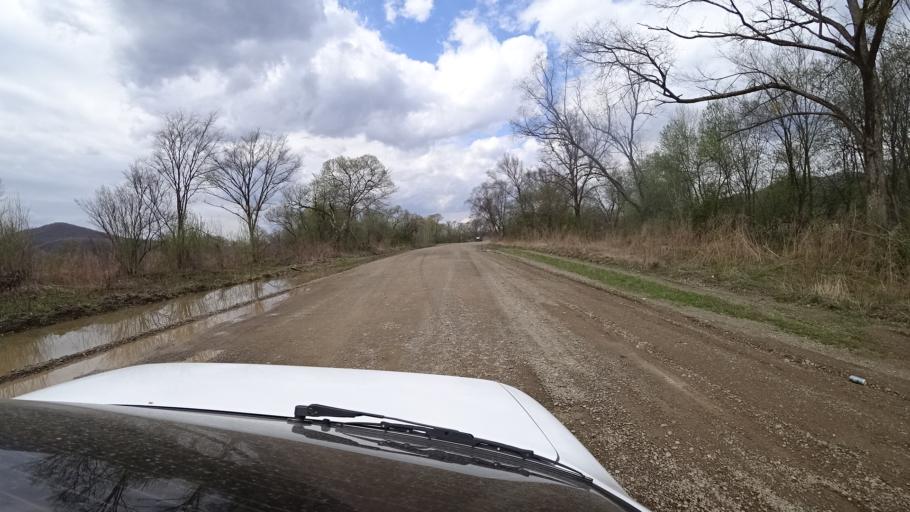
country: RU
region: Primorskiy
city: Novopokrovka
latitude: 45.6107
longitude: 134.2752
